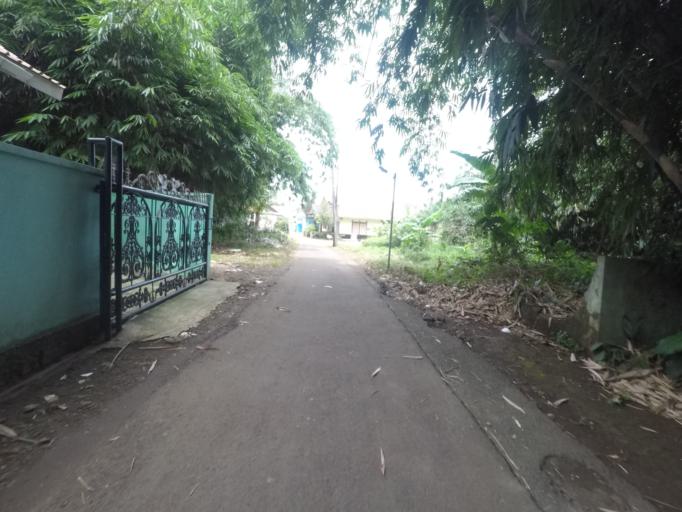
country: ID
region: West Java
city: Ciampea
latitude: -6.5496
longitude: 106.7478
